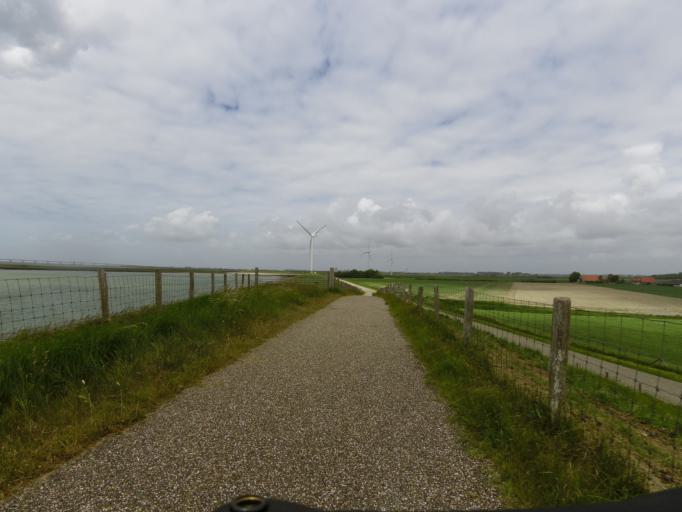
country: NL
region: Zeeland
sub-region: Gemeente Goes
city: Goes
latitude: 51.6220
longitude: 3.9550
